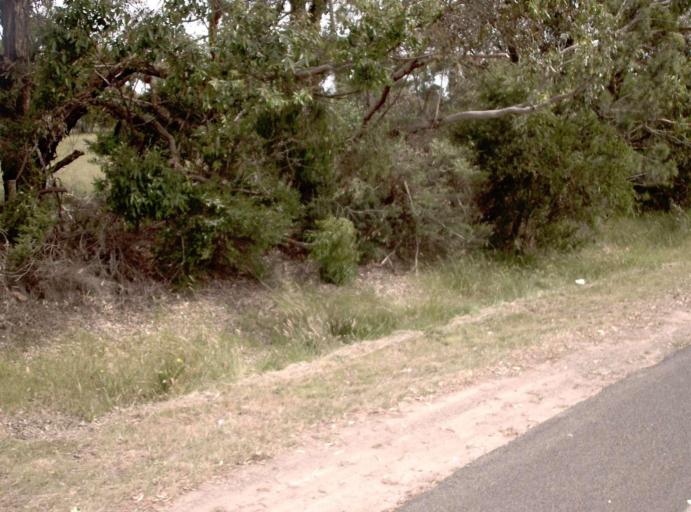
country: AU
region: Victoria
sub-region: Mornington Peninsula
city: Moorooduc
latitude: -38.2298
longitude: 145.0944
